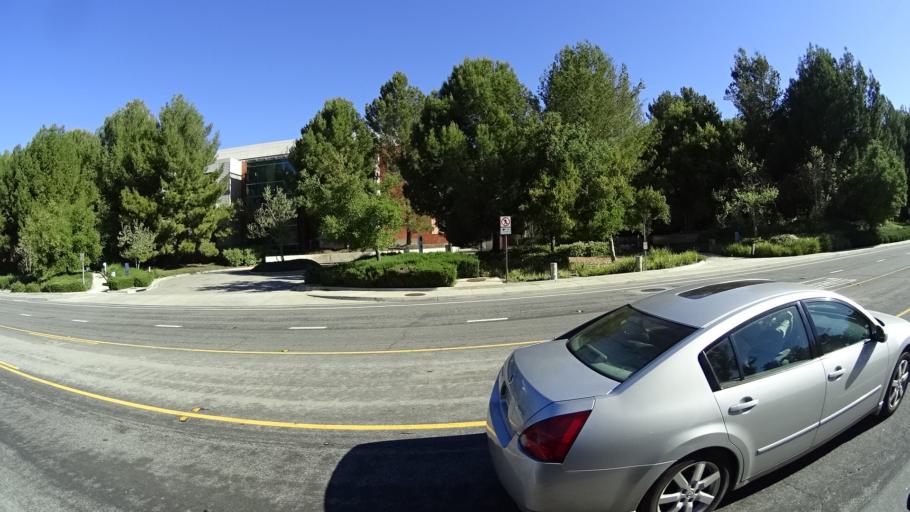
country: US
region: California
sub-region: Ventura County
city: Casa Conejo
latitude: 34.1869
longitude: -118.9231
